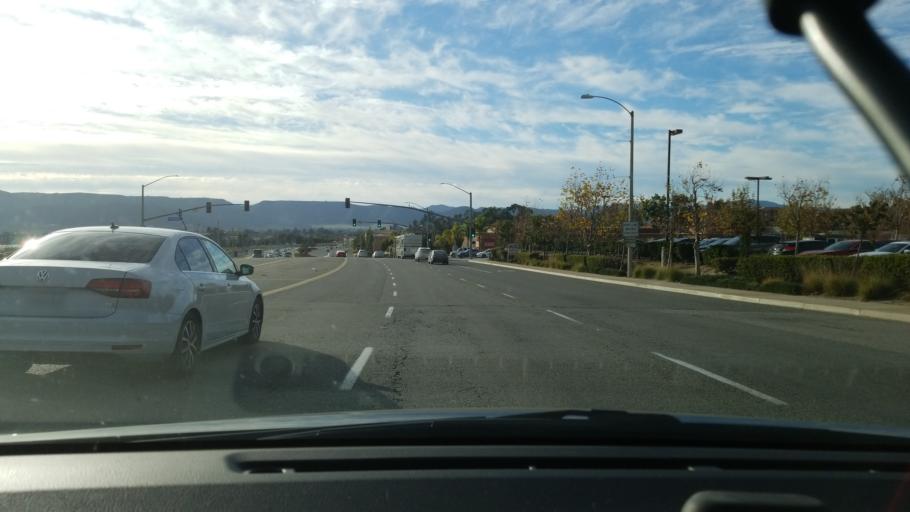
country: US
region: California
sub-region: Riverside County
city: Murrieta Hot Springs
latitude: 33.5562
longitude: -117.1830
